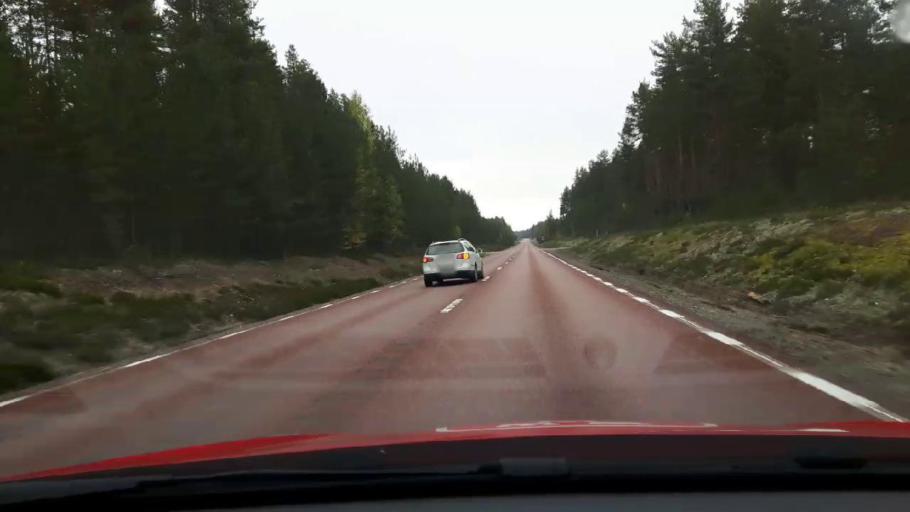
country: SE
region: Gaevleborg
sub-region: Ljusdals Kommun
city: Farila
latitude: 61.8137
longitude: 15.7659
